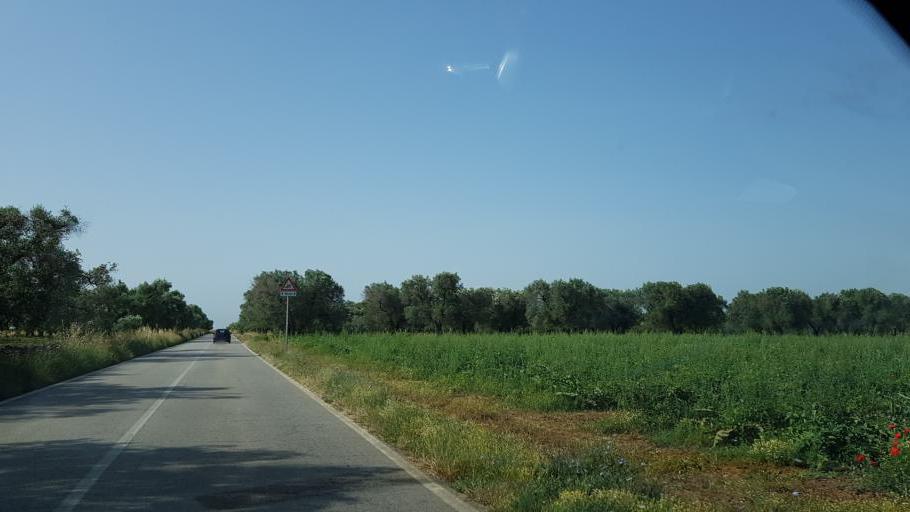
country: IT
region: Apulia
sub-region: Provincia di Brindisi
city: Mesagne
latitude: 40.5144
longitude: 17.8263
